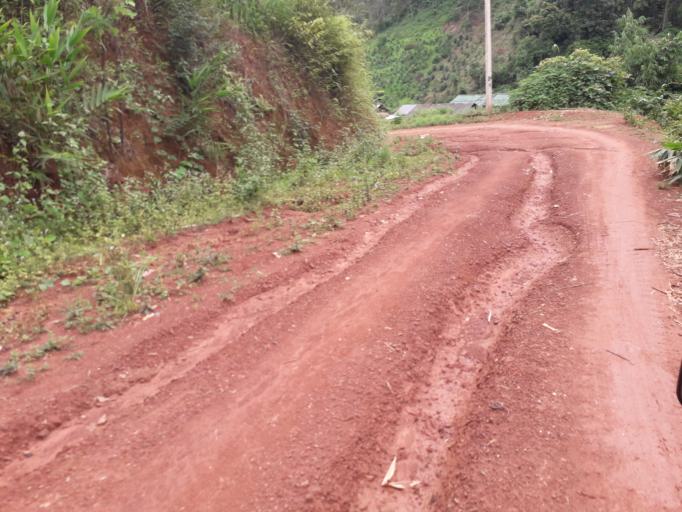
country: CN
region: Yunnan
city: Menglie
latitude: 22.2011
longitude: 101.6733
